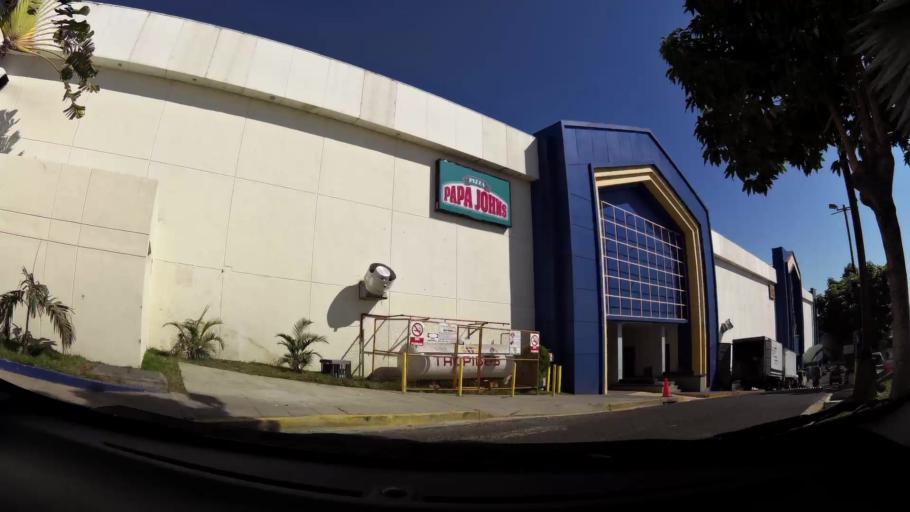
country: SV
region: La Libertad
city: Santa Tecla
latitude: 13.6782
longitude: -89.2758
